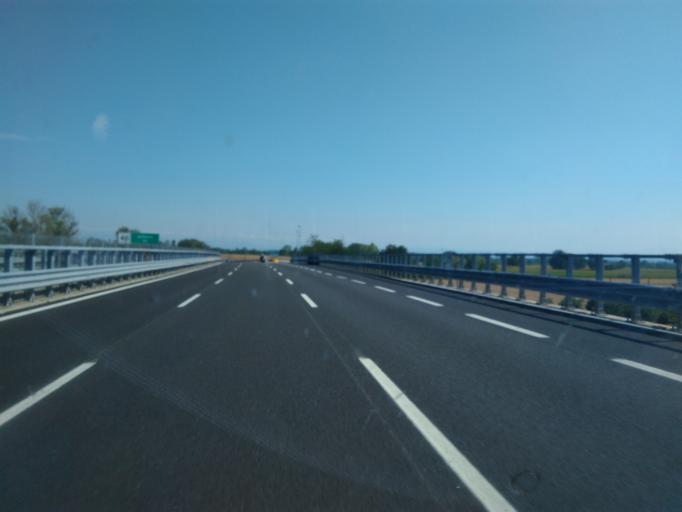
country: IT
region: Piedmont
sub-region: Provincia di Alessandria
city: Castellazzo Bormida
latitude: 44.8780
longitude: 8.5700
